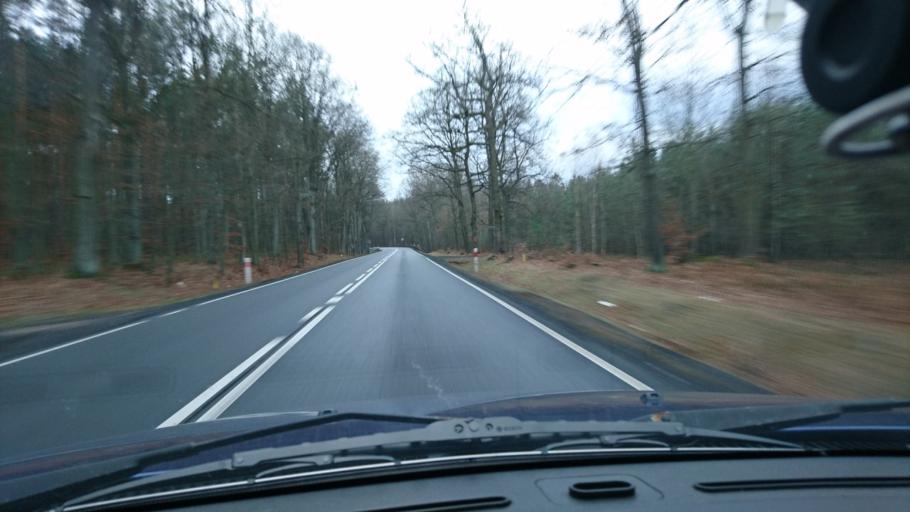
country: PL
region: Opole Voivodeship
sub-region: Powiat oleski
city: Olesno
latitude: 50.9351
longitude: 18.3311
